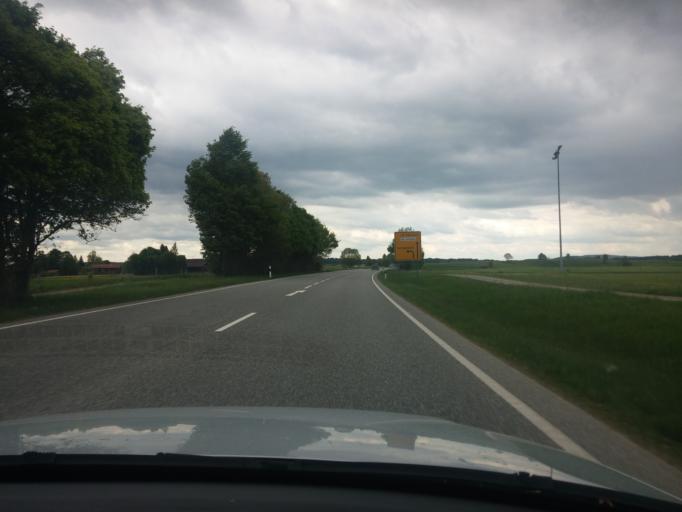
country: DE
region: Bavaria
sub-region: Upper Bavaria
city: Sachsenkam
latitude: 47.7978
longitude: 11.6398
